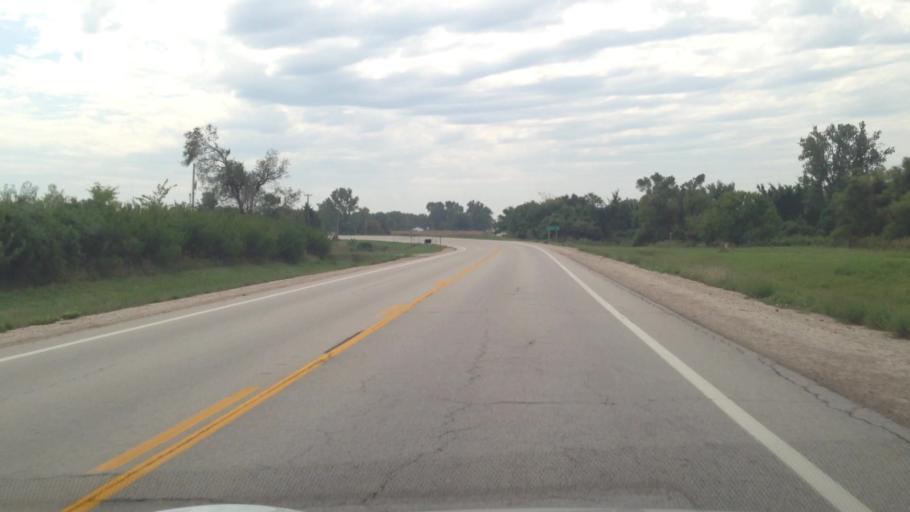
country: US
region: Kansas
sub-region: Anderson County
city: Garnett
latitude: 38.0871
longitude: -95.2434
